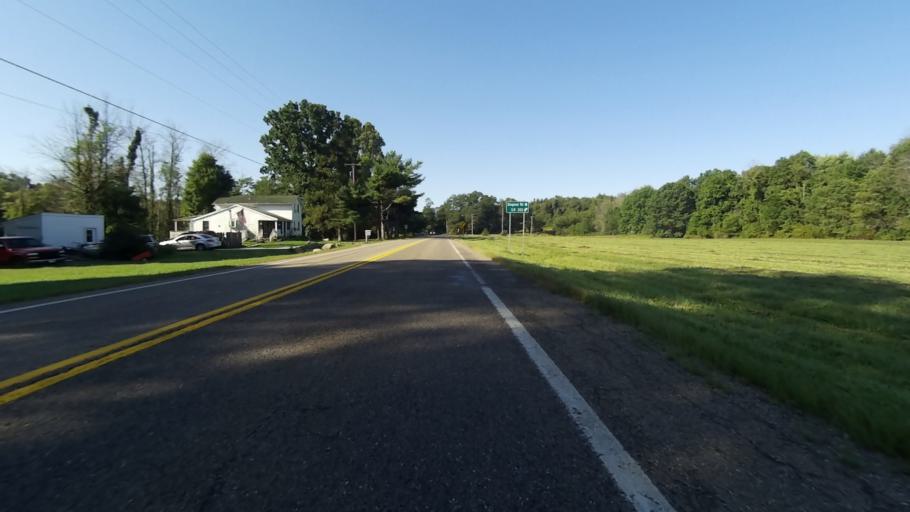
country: US
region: Ohio
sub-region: Portage County
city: Streetsboro
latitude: 41.2399
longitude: -81.3025
